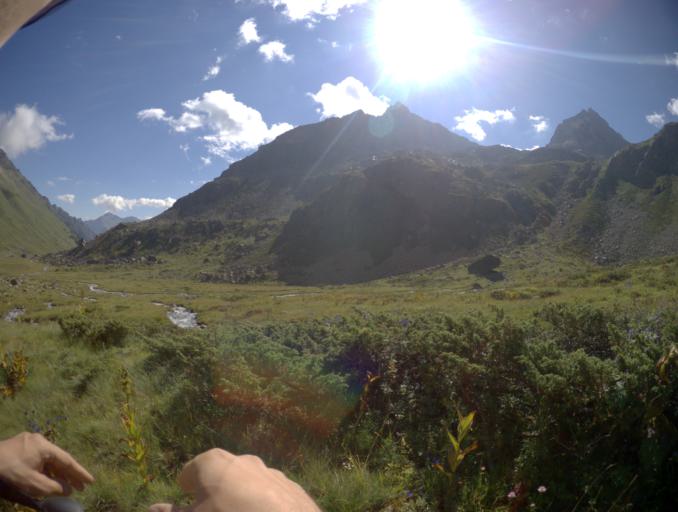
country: RU
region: Karachayevo-Cherkesiya
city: Uchkulan
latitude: 43.3273
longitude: 42.1096
